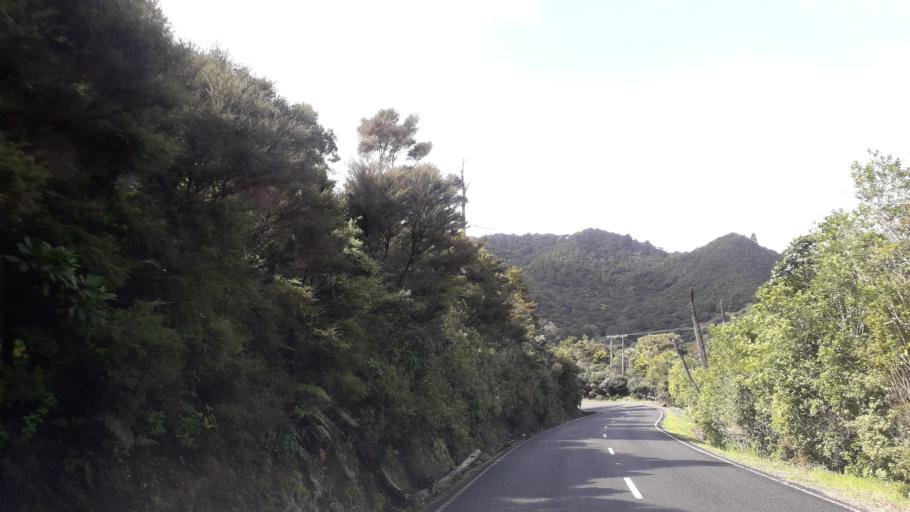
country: NZ
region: Northland
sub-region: Far North District
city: Paihia
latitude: -35.2546
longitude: 174.2643
